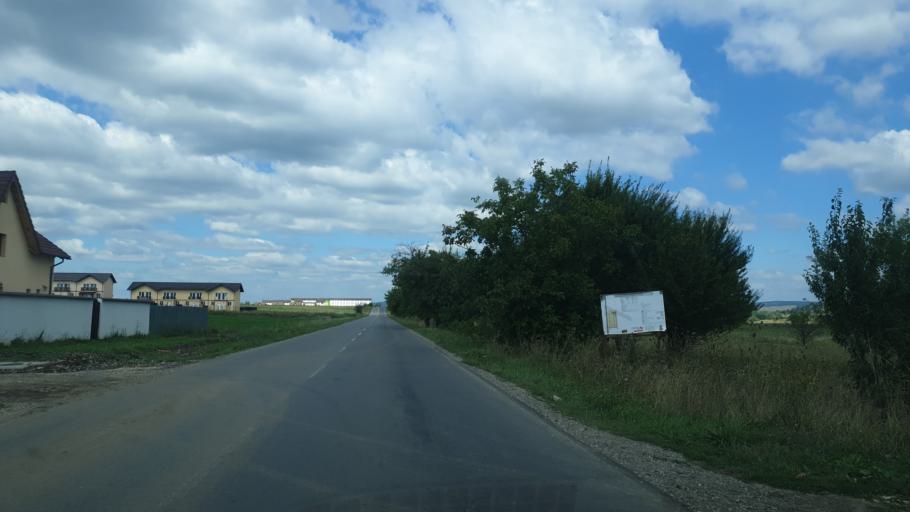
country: RO
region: Brasov
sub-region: Comuna Sanpetru
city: Sanpetru
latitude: 45.7207
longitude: 25.6277
